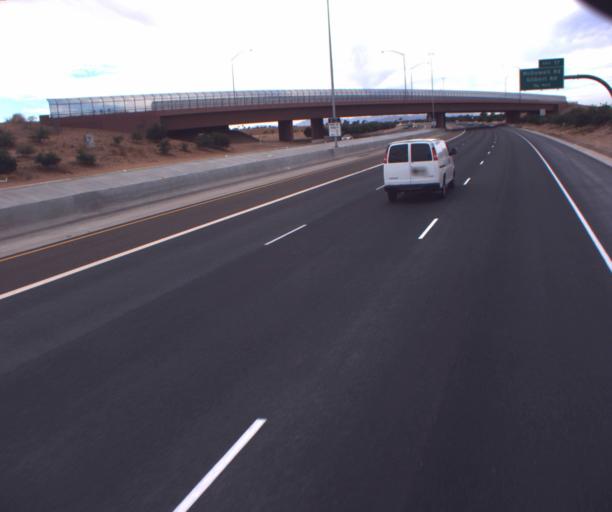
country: US
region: Arizona
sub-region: Maricopa County
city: Mesa
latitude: 33.4818
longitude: -111.7672
